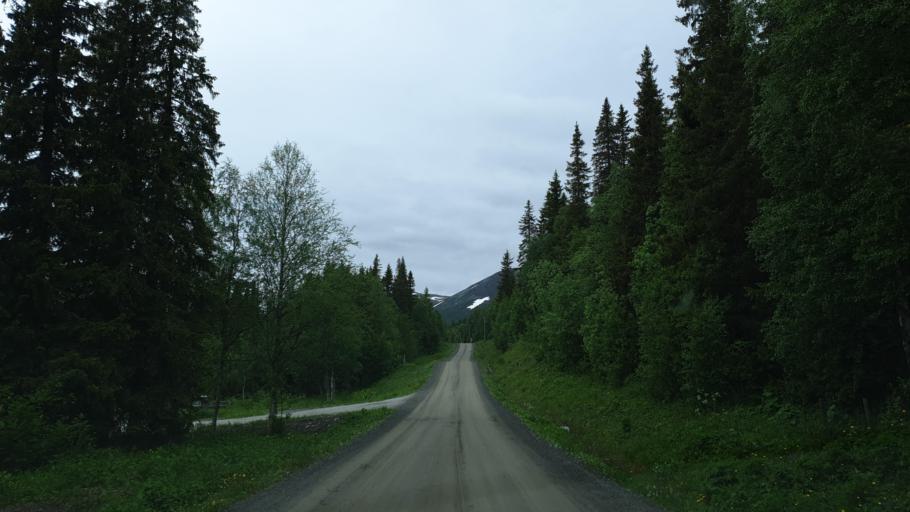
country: SE
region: Vaesterbotten
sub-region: Vilhelmina Kommun
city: Sjoberg
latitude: 65.3494
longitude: 15.8530
